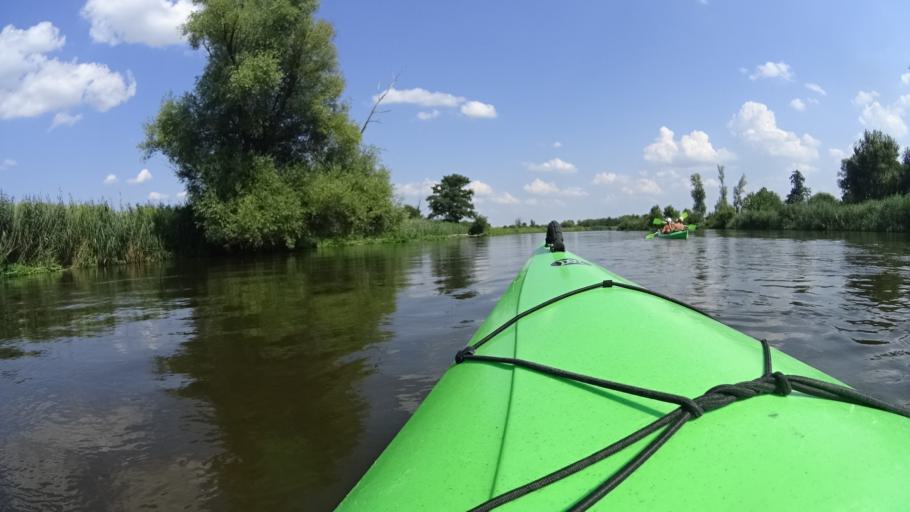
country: PL
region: Masovian Voivodeship
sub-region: Powiat bialobrzeski
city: Wysmierzyce
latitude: 51.6574
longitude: 20.8371
